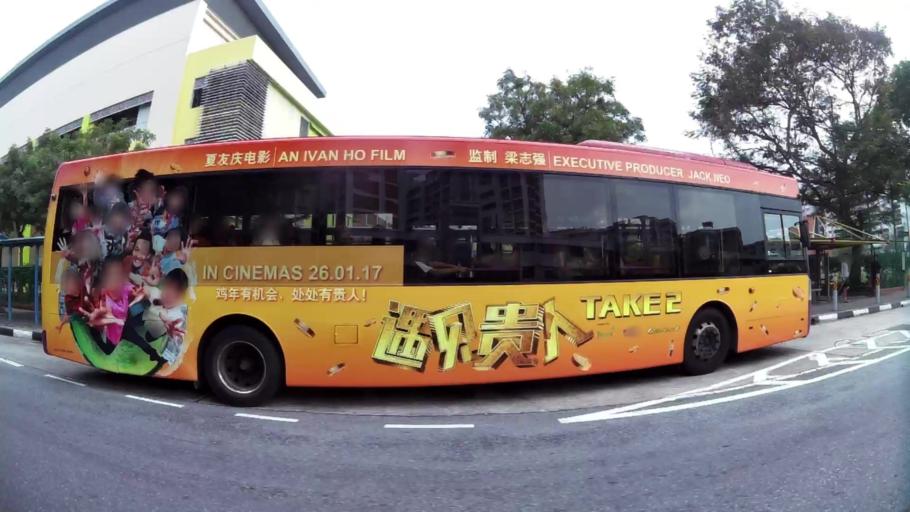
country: SG
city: Singapore
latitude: 1.3477
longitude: 103.9384
